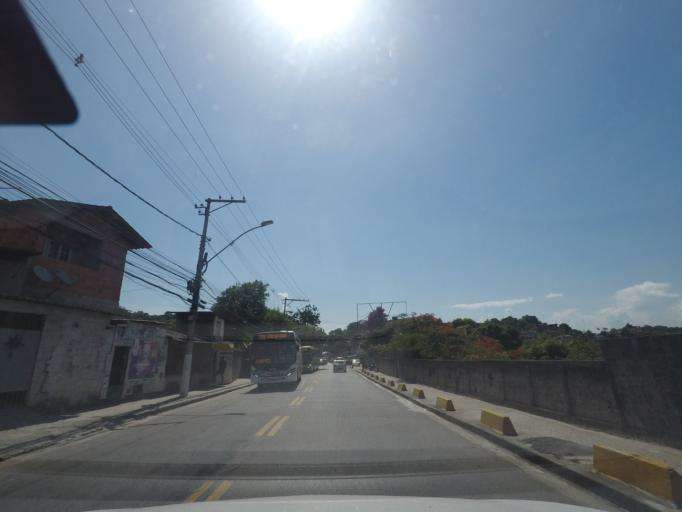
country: BR
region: Rio de Janeiro
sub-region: Niteroi
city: Niteroi
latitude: -22.9104
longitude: -43.0501
